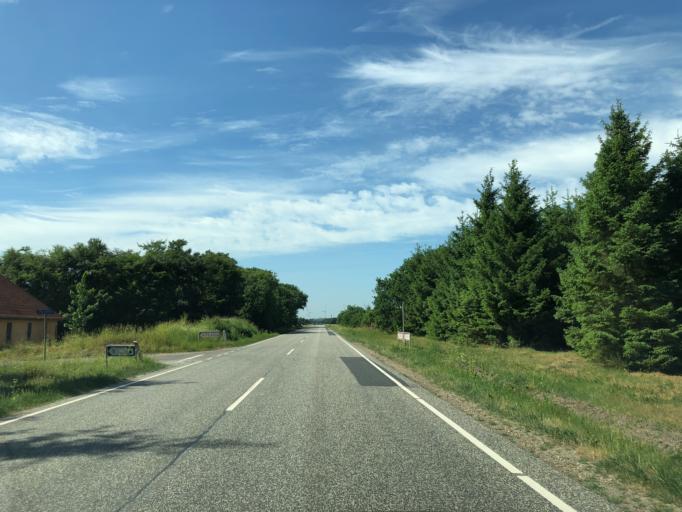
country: DK
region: South Denmark
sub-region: Vejle Kommune
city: Give
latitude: 55.8926
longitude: 9.2114
